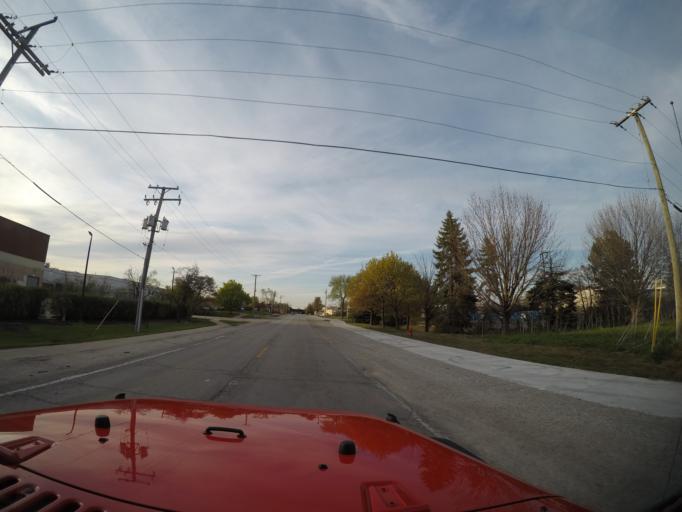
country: US
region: Illinois
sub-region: Cook County
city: Northbrook
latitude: 42.0992
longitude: -87.8295
